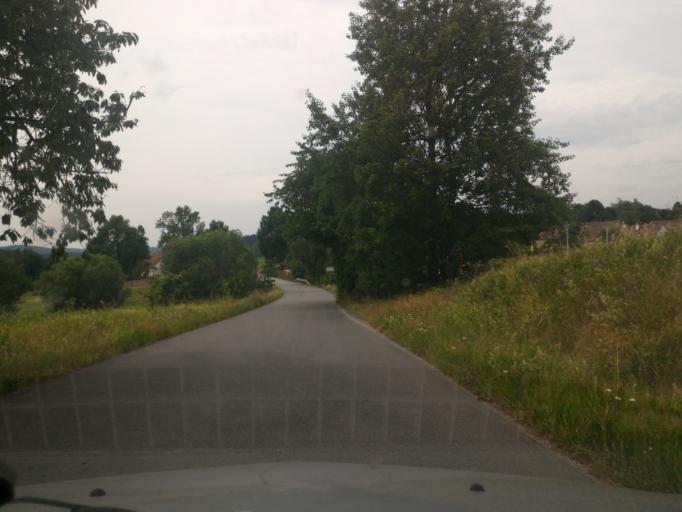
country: CZ
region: Vysocina
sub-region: Okres Jihlava
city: Telc
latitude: 49.2086
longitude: 15.3902
